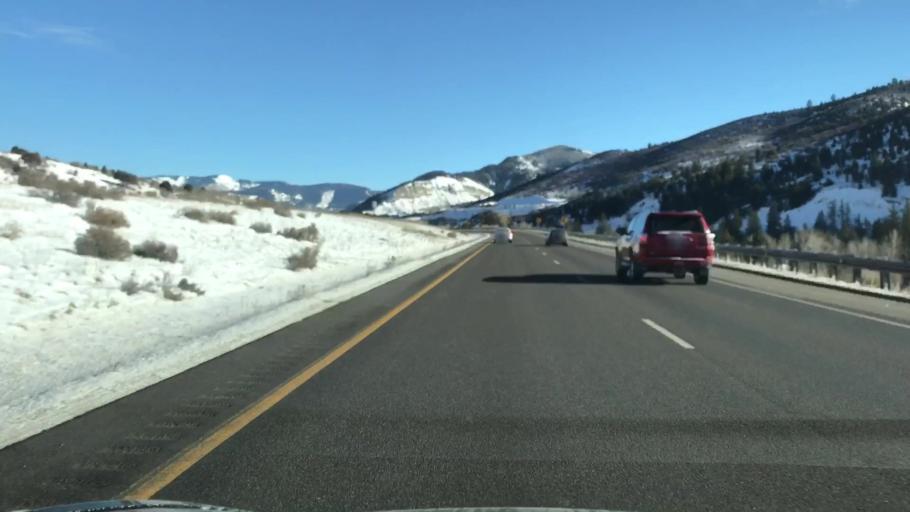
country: US
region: Colorado
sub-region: Eagle County
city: Avon
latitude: 39.6394
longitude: -106.5498
